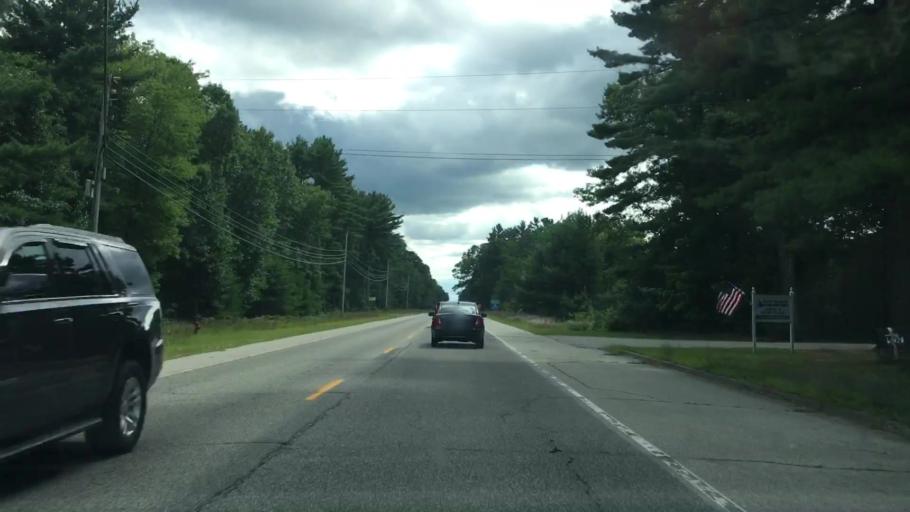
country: US
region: Maine
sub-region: York County
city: North Berwick
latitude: 43.3396
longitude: -70.7326
